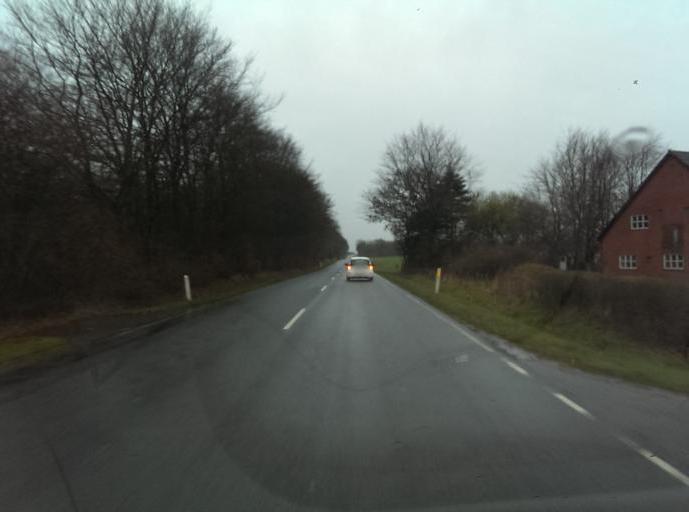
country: DK
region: South Denmark
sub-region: Esbjerg Kommune
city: Tjaereborg
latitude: 55.4956
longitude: 8.5774
